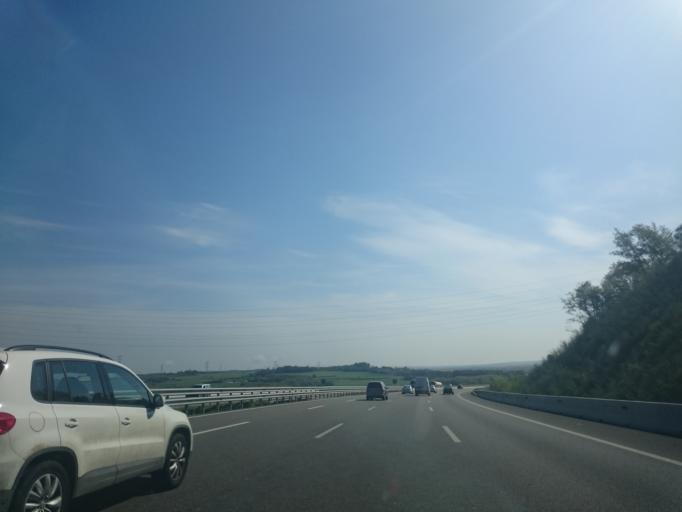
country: ES
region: Catalonia
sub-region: Provincia de Girona
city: Sant Julia de Ramis
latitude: 42.0430
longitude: 2.8449
